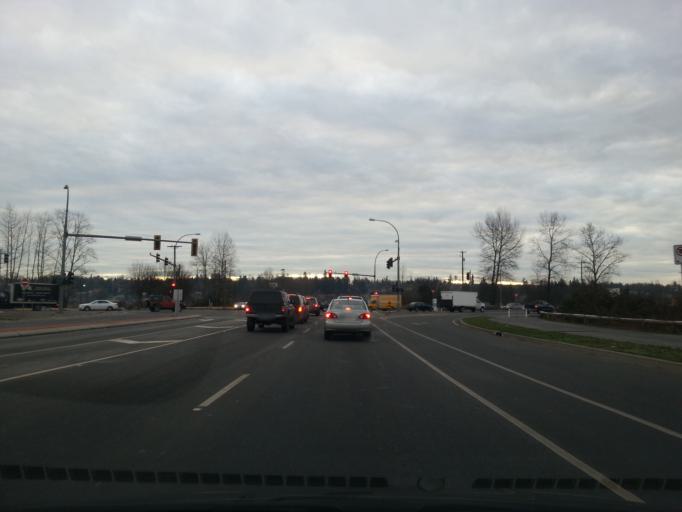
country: CA
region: British Columbia
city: Langley
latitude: 49.1384
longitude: -122.7357
